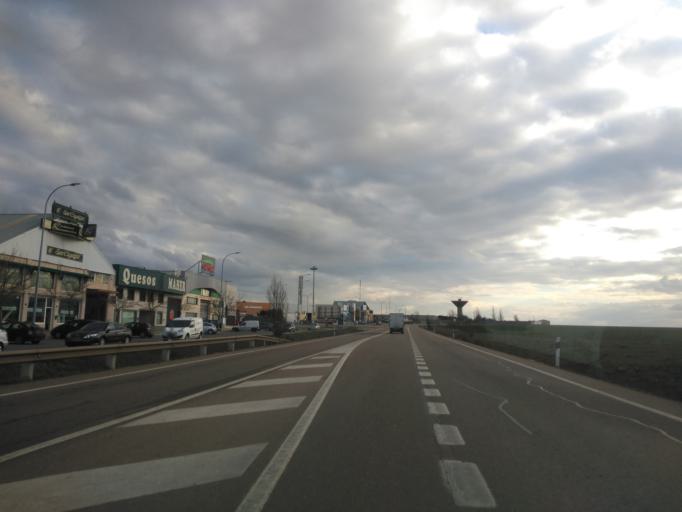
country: ES
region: Castille and Leon
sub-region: Provincia de Salamanca
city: Carbajosa de la Sagrada
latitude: 40.9384
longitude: -5.6685
